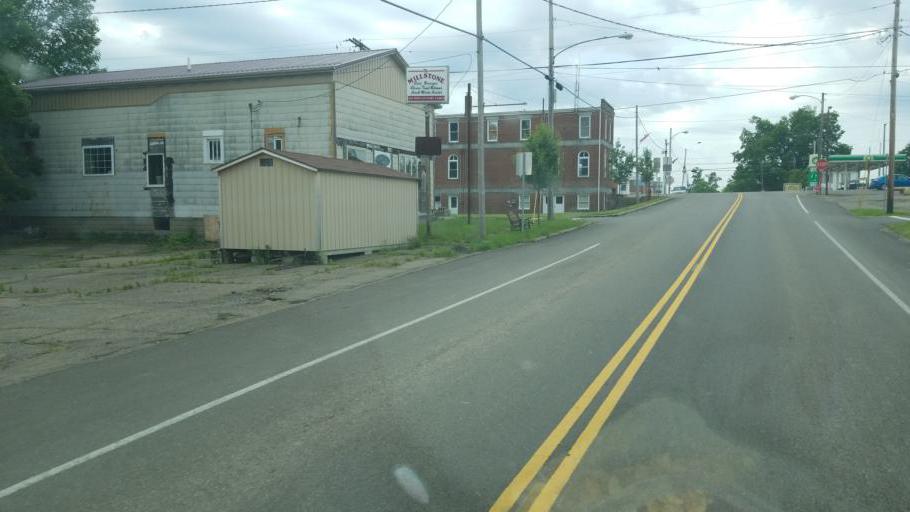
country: US
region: Ohio
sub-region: Knox County
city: Danville
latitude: 40.4520
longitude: -82.2601
